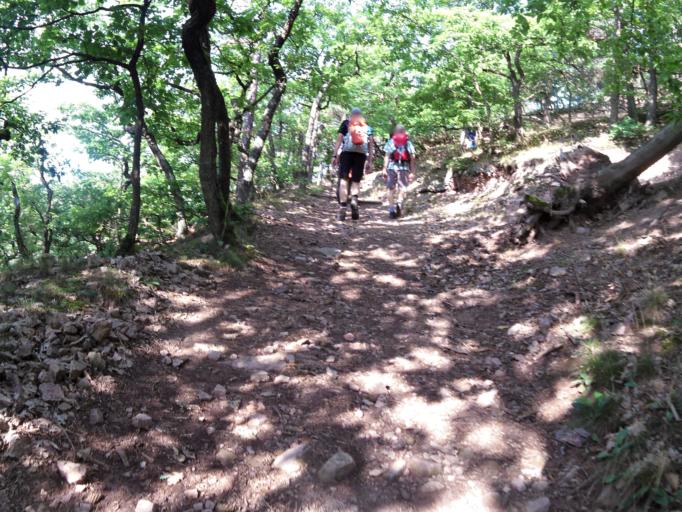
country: DE
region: Rheinland-Pfalz
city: Bad Munster am Stein-Ebernburg
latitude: 49.8166
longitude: 7.8421
